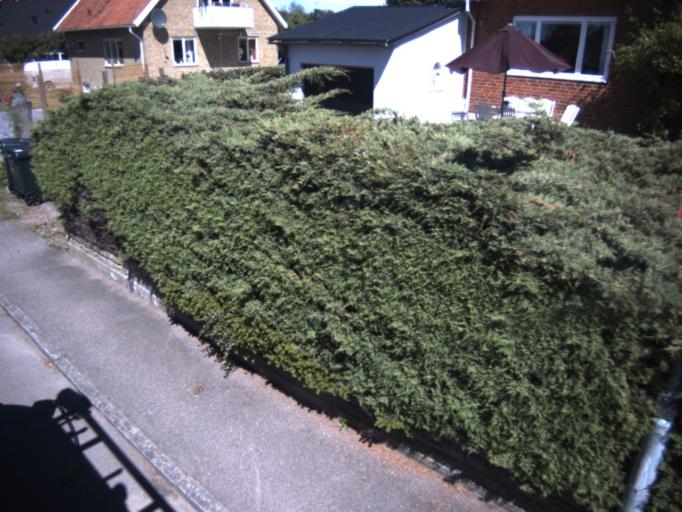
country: SE
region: Skane
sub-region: Helsingborg
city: Morarp
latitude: 56.0603
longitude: 12.8782
